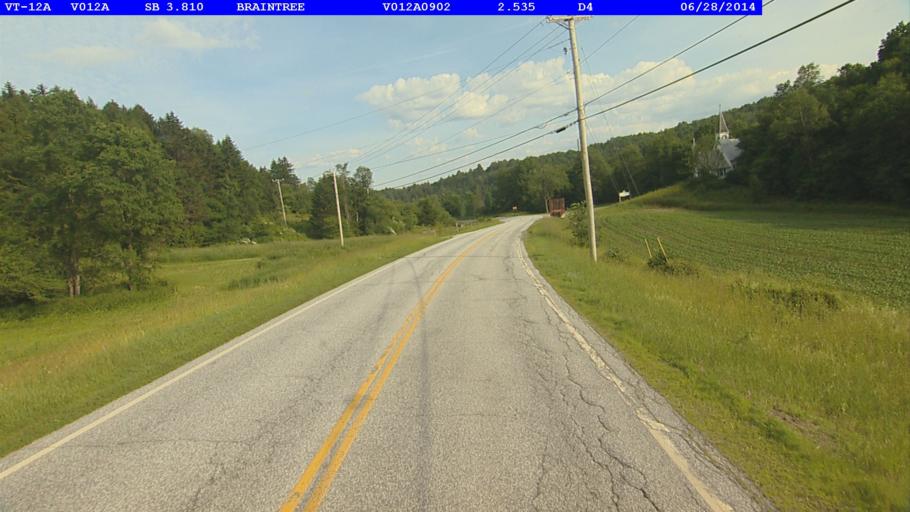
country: US
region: Vermont
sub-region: Orange County
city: Randolph
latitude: 43.9531
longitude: -72.7210
